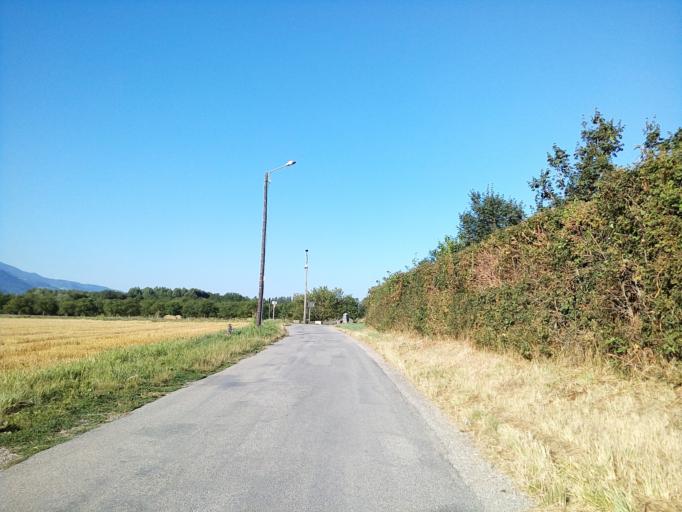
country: FR
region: Rhone-Alpes
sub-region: Departement de l'Isere
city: La Terrasse
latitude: 45.3242
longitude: 5.9382
